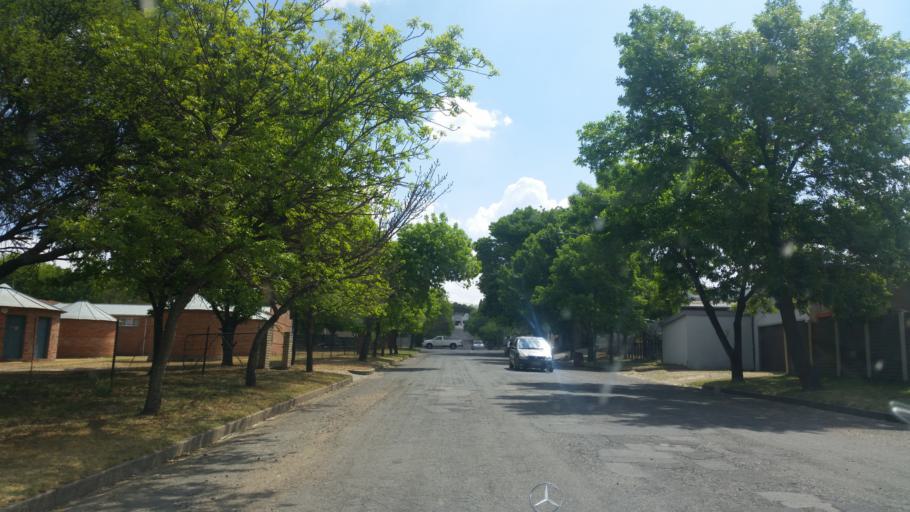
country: ZA
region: Orange Free State
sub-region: Thabo Mofutsanyana District Municipality
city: Reitz
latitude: -27.8033
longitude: 28.4285
